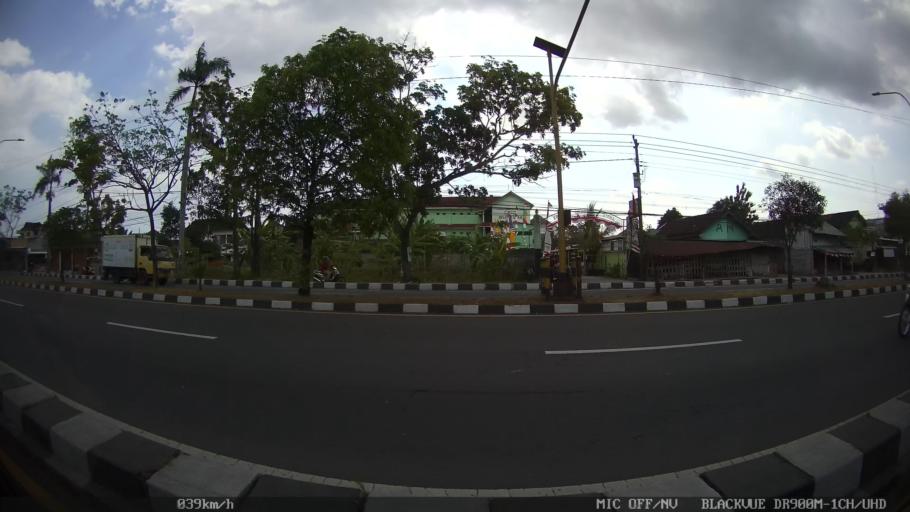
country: ID
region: Daerah Istimewa Yogyakarta
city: Kasihan
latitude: -7.8124
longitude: 110.3248
